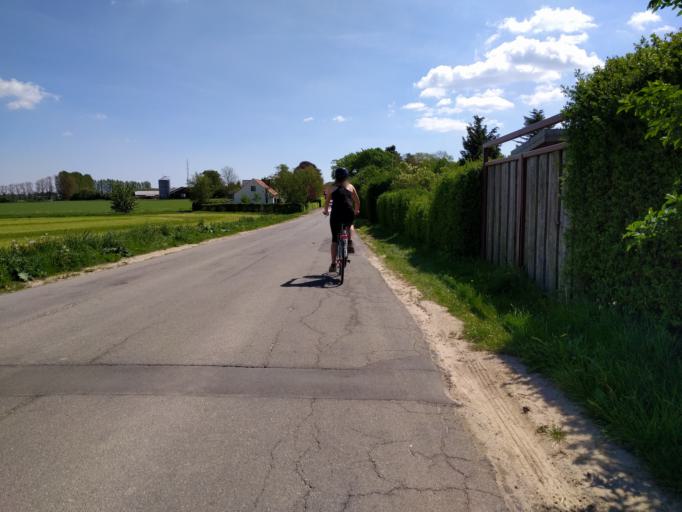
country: DK
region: Zealand
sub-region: Guldborgsund Kommune
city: Nykobing Falster
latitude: 54.7454
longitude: 11.9514
